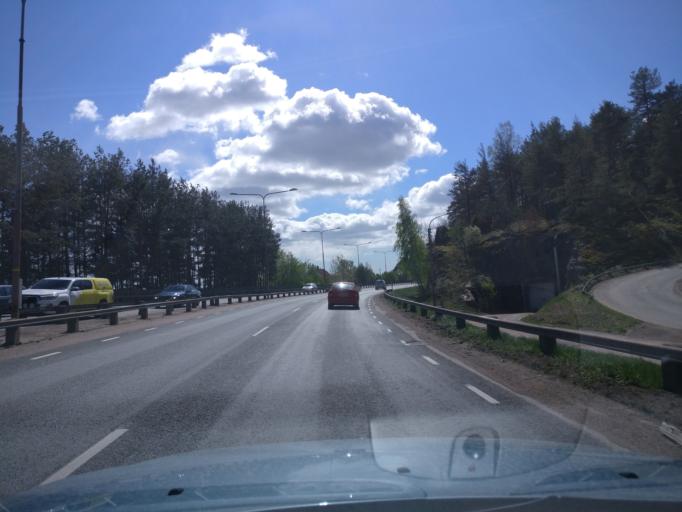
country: SE
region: Vaermland
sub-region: Karlstads Kommun
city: Karlstad
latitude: 59.3963
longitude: 13.5349
